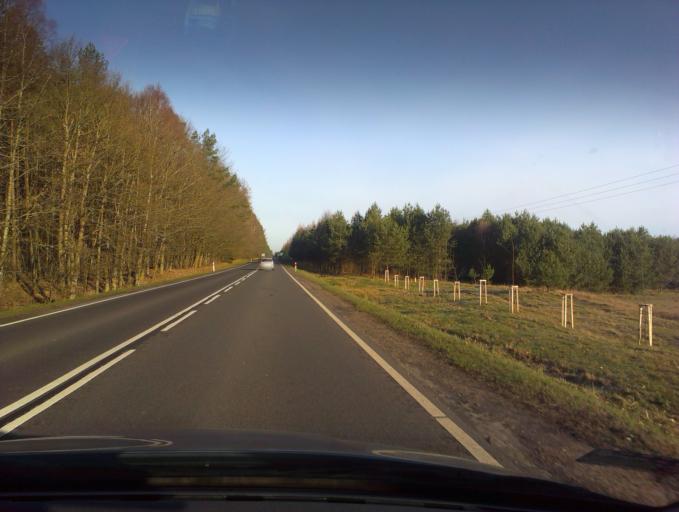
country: PL
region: West Pomeranian Voivodeship
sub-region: Powiat koszalinski
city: Sianow
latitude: 54.0955
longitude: 16.3596
